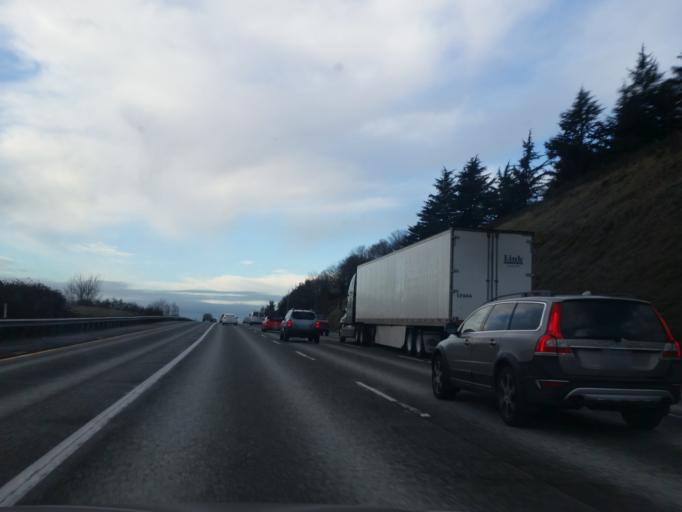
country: US
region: Washington
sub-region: King County
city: Boulevard Park
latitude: 47.5373
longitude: -122.2982
